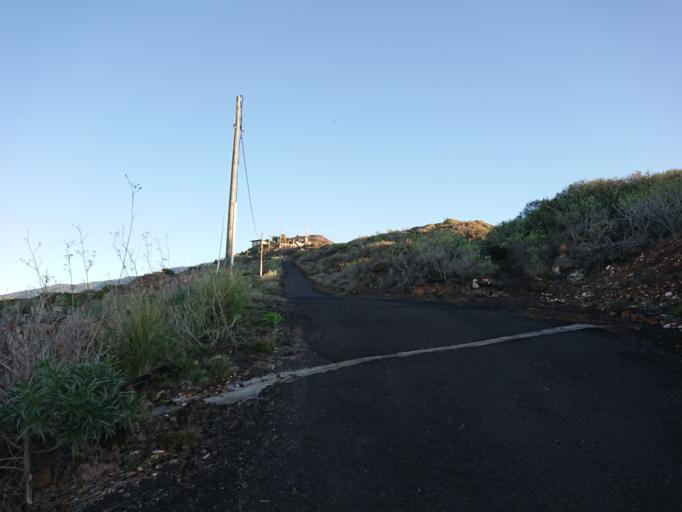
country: ES
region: Canary Islands
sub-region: Provincia de Santa Cruz de Tenerife
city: Tazacorte
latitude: 28.6605
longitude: -17.9435
